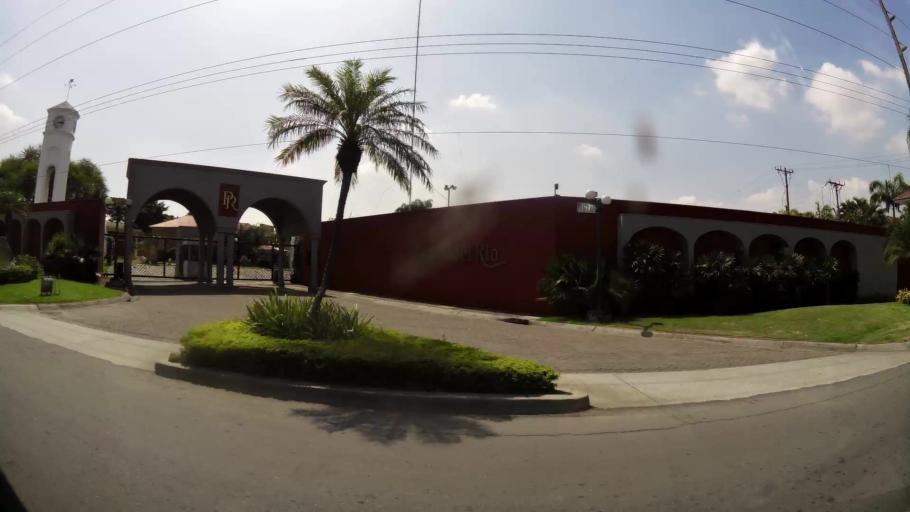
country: EC
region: Guayas
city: Eloy Alfaro
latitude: -2.1237
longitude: -79.8643
